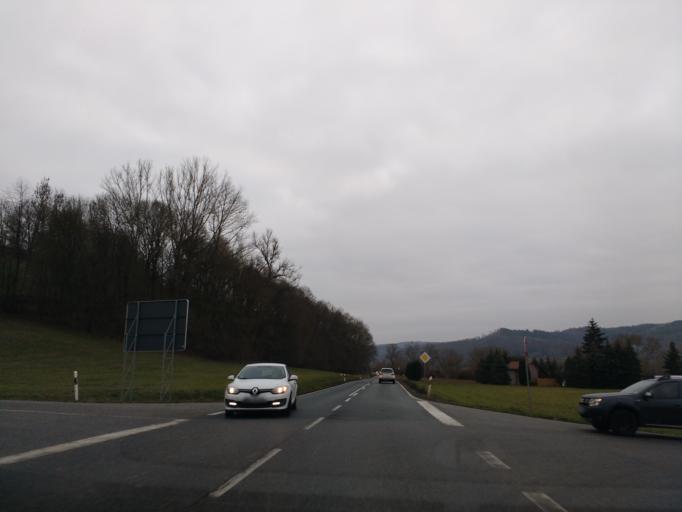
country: DE
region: Hesse
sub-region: Regierungsbezirk Kassel
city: Alheim
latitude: 51.0286
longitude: 9.6842
